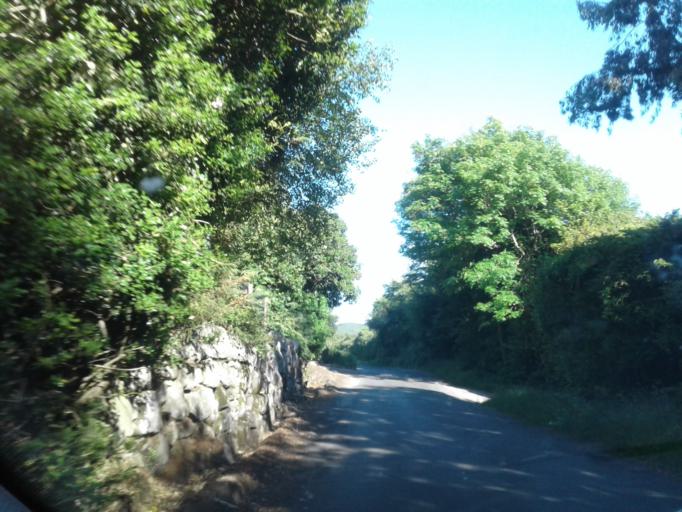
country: IE
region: Leinster
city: Ballinteer
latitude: 53.1909
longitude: -6.2606
